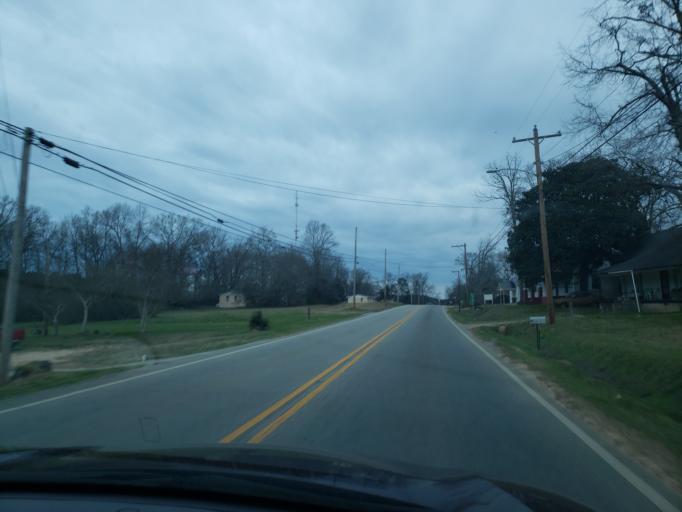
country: US
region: Alabama
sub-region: Chambers County
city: Lafayette
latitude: 32.9125
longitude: -85.4006
